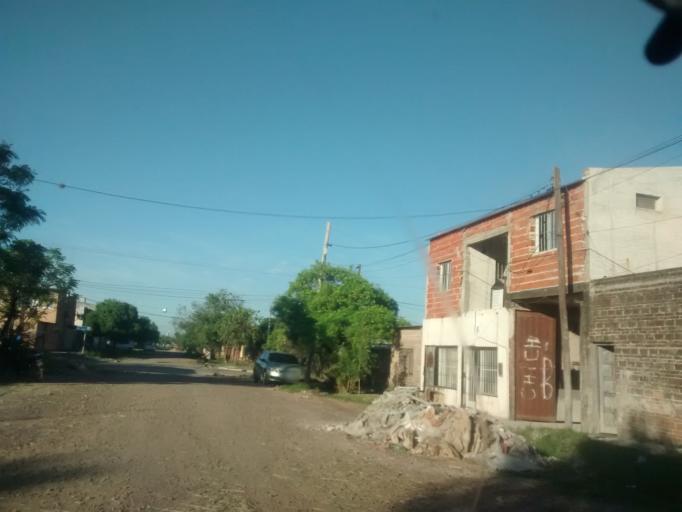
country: AR
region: Chaco
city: Resistencia
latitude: -27.4520
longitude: -59.0090
